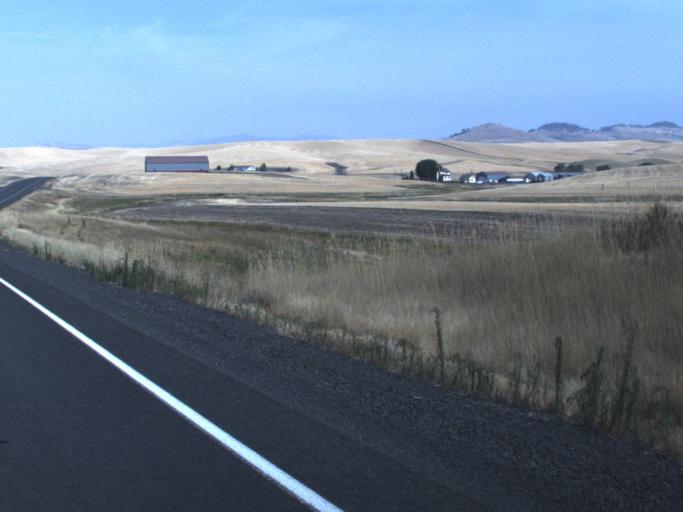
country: US
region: Washington
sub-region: Whitman County
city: Pullman
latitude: 46.8214
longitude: -117.1167
